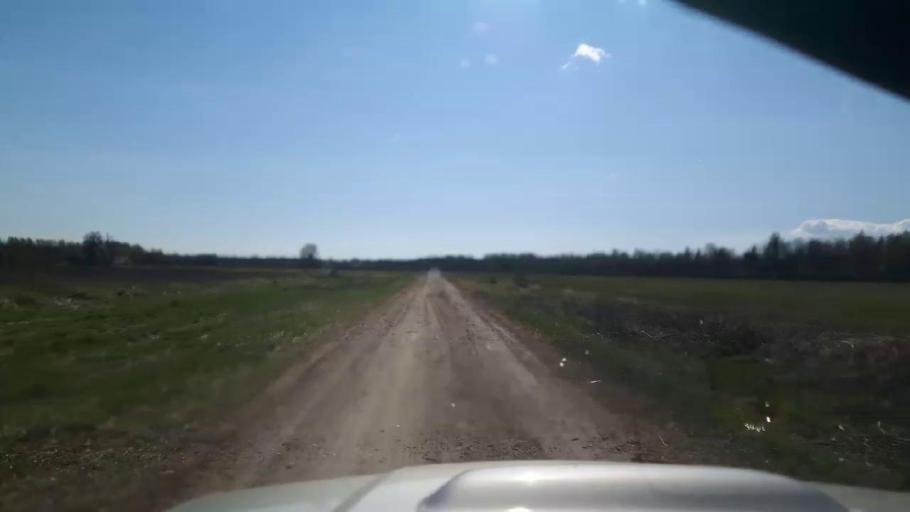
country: EE
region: Paernumaa
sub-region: Tootsi vald
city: Tootsi
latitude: 58.4410
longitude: 24.8756
